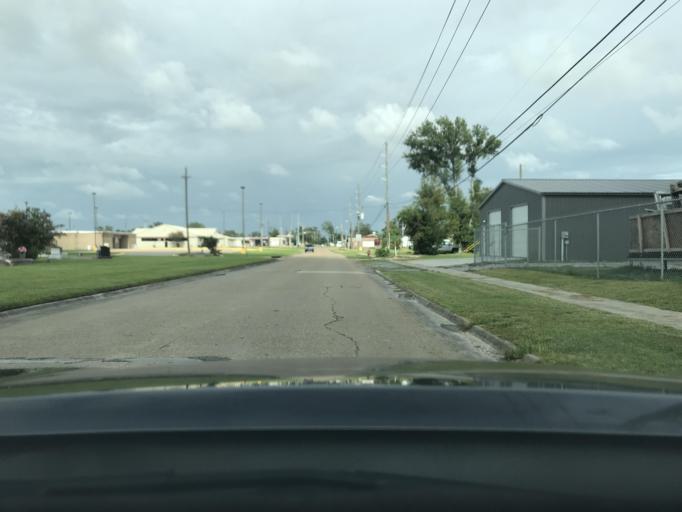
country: US
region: Louisiana
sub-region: Calcasieu Parish
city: Westlake
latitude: 30.2477
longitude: -93.2608
